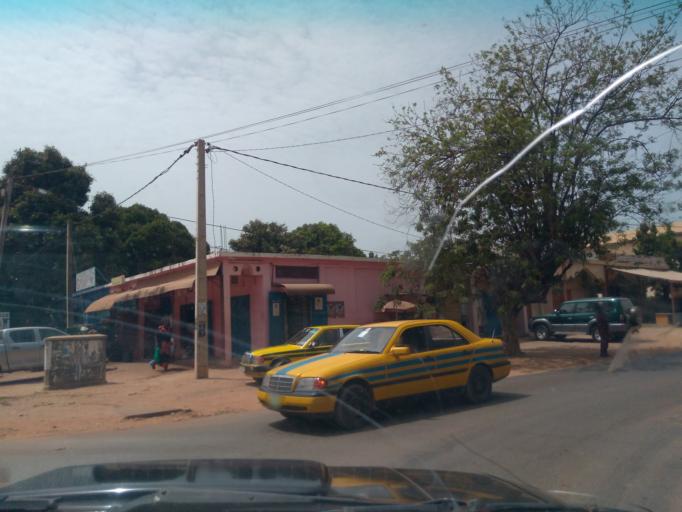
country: GM
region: Banjul
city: Bakau
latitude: 13.4679
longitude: -16.6913
